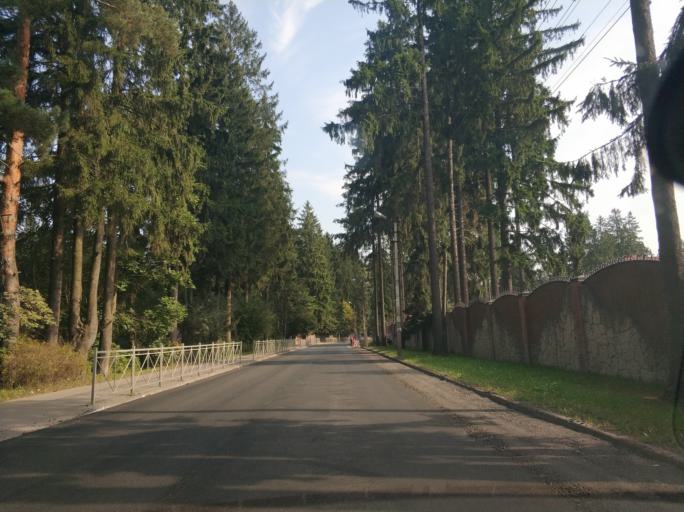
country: RU
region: Leningrad
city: Vsevolozhsk
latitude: 60.0204
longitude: 30.6625
